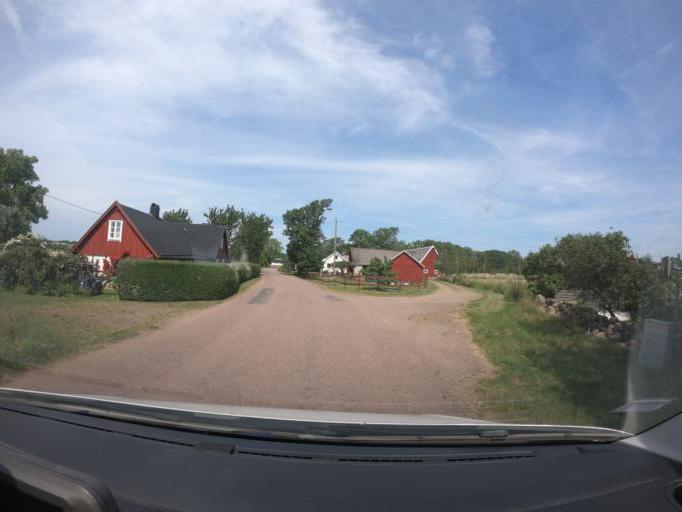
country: SE
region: Skane
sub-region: Angelholms Kommun
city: Vejbystrand
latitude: 56.3966
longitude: 12.7209
